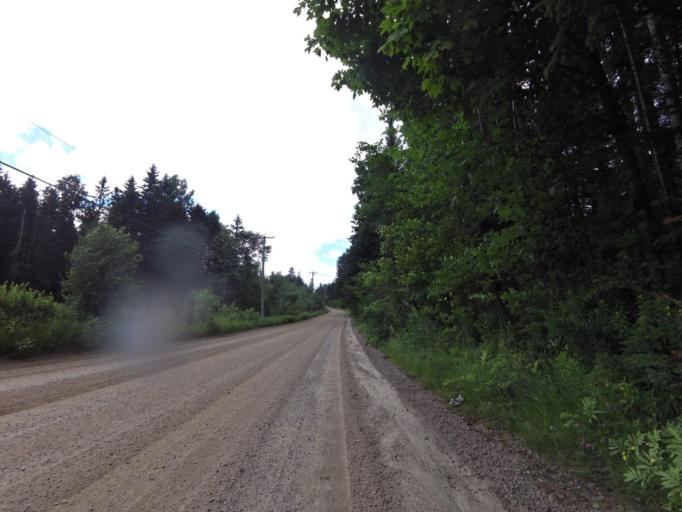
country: CA
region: Quebec
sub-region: Laurentides
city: Mont-Tremblant
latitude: 45.9519
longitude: -74.5936
